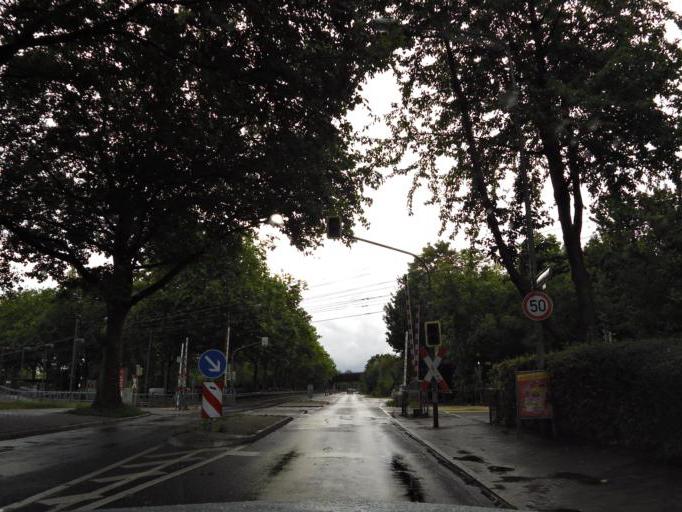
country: DE
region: Hesse
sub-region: Regierungsbezirk Darmstadt
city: Bad Homburg vor der Hoehe
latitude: 50.1836
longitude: 8.6595
